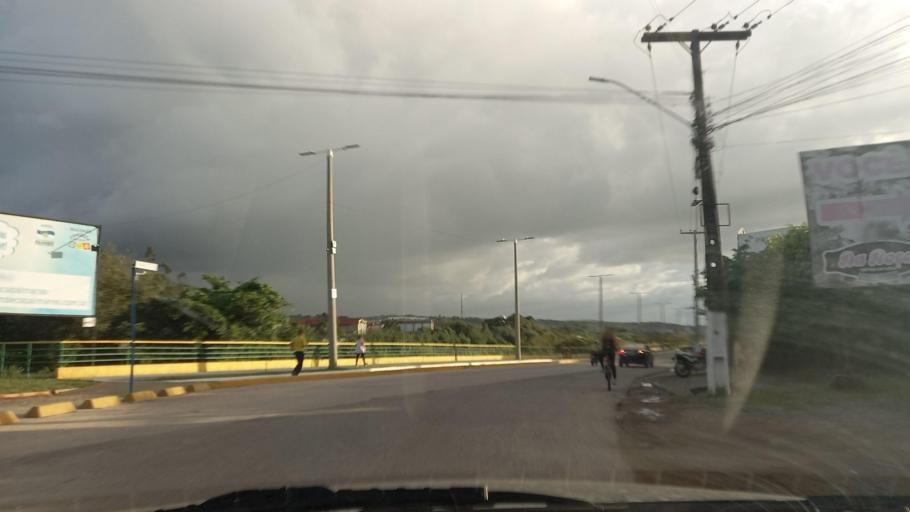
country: BR
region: Pernambuco
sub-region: Palmares
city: Palmares
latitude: -8.6785
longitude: -35.5776
